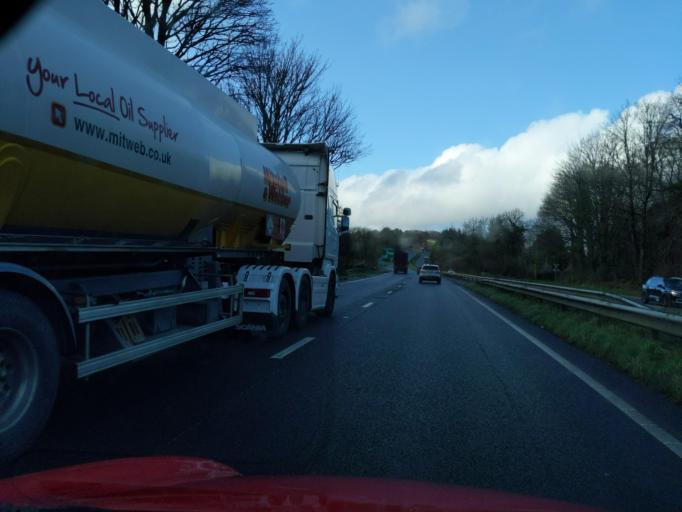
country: GB
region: England
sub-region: Cornwall
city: Liskeard
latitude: 50.4192
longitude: -4.3994
